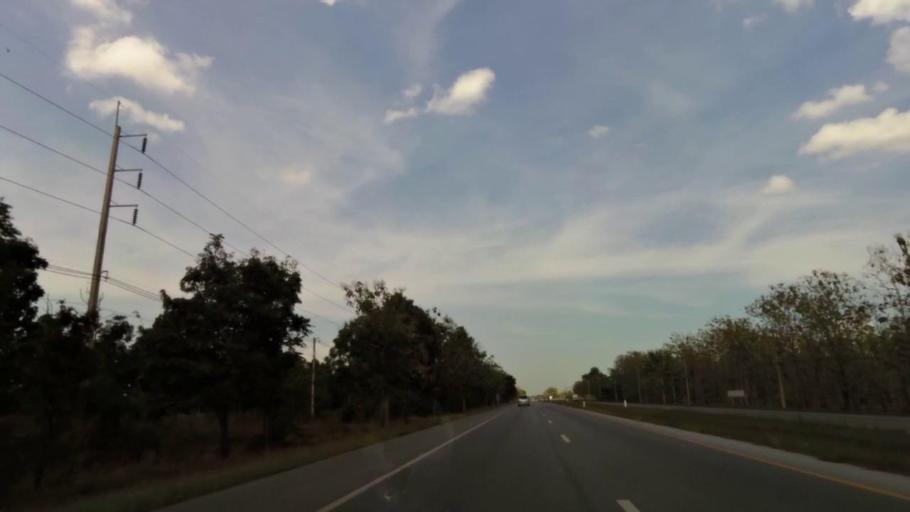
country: TH
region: Uttaradit
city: Thong Saen Khan
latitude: 17.5095
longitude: 100.2255
